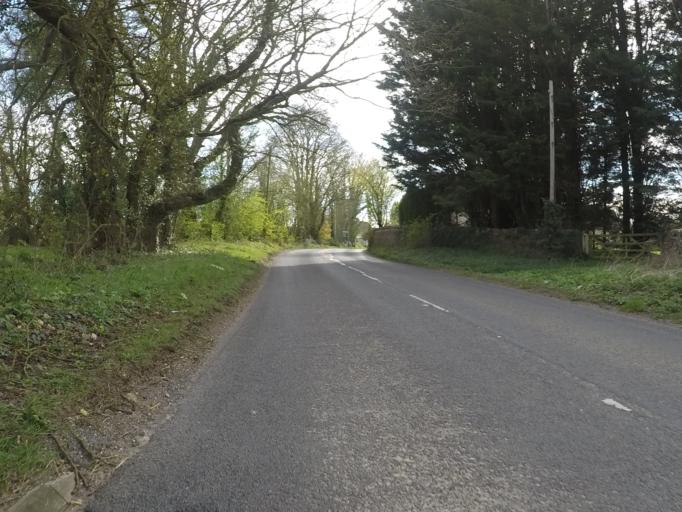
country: GB
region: England
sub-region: Oxfordshire
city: Charlbury
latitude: 51.8485
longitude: -1.4757
